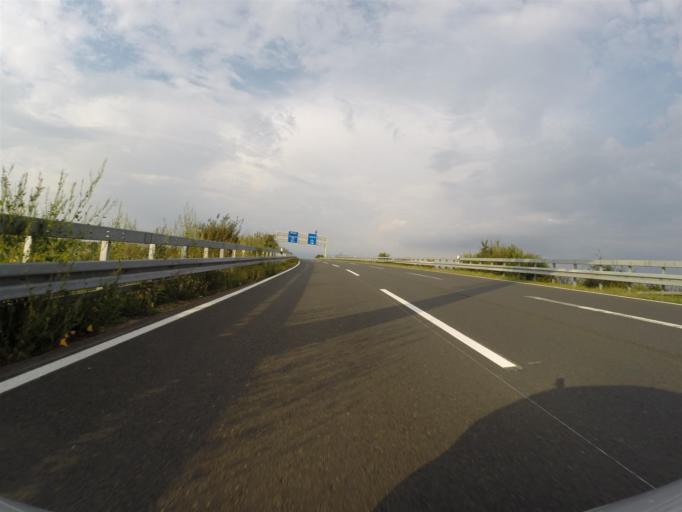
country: DE
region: Saxony-Anhalt
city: Grosskorbetha
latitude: 51.2328
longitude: 12.0559
